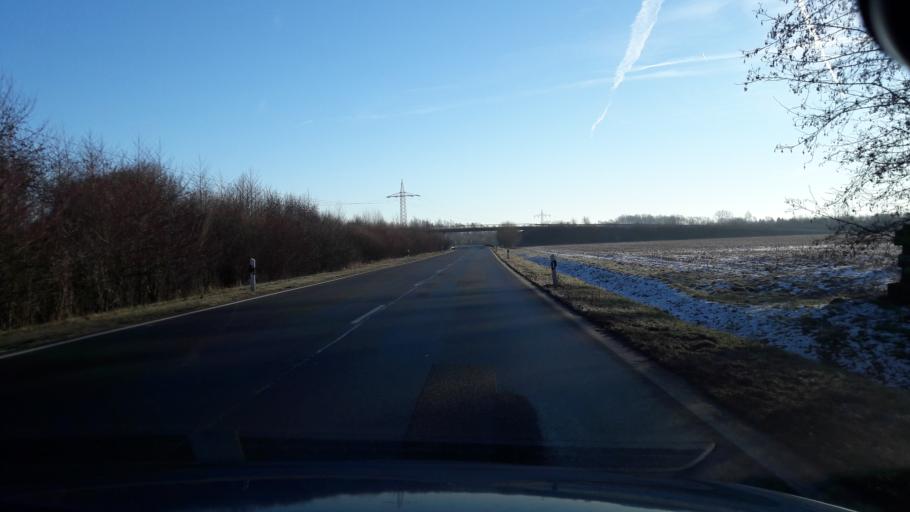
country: DE
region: North Rhine-Westphalia
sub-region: Regierungsbezirk Detmold
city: Langenberg
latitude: 51.7319
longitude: 8.3246
